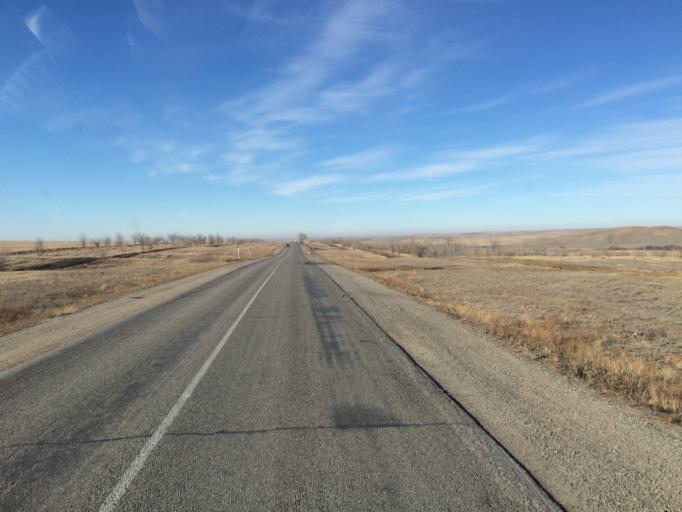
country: KZ
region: Aqtoebe
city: Aqtobe
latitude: 50.2821
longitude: 57.7456
